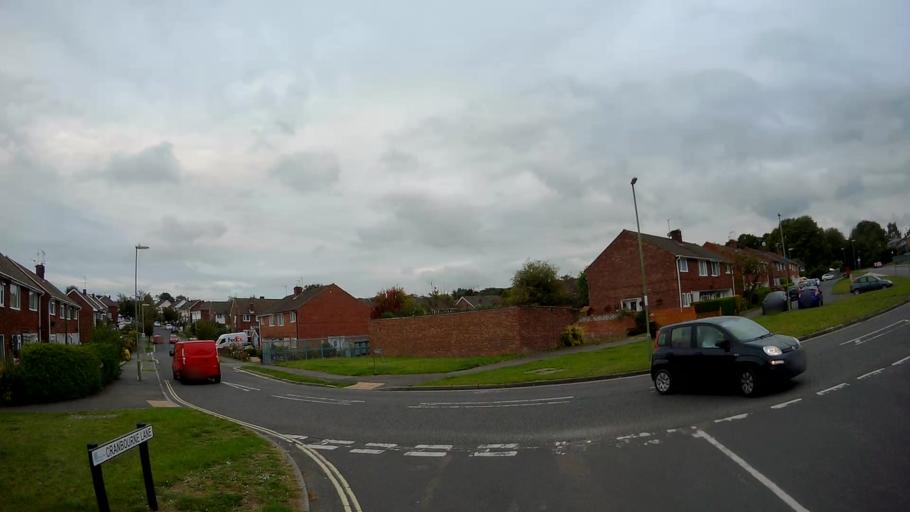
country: GB
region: England
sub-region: Hampshire
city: Basingstoke
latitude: 51.2514
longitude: -1.0989
